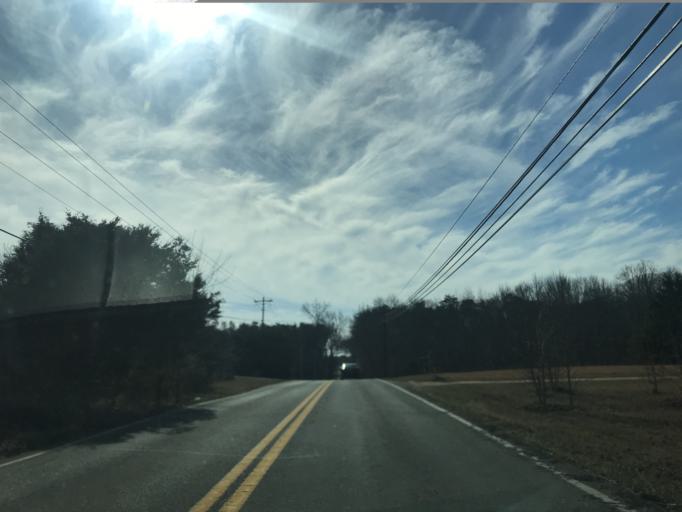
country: US
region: Maryland
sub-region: Charles County
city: Potomac Heights
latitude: 38.5711
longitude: -77.1266
